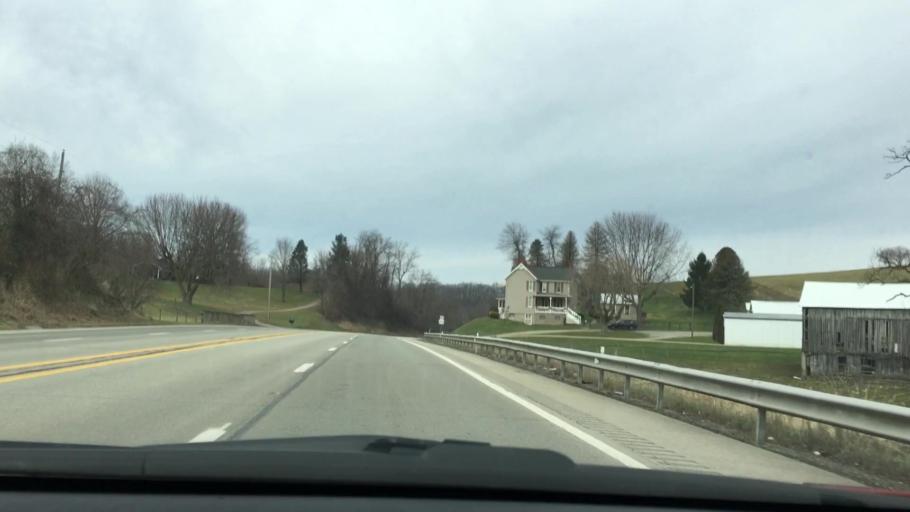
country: US
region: Pennsylvania
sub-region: Fayette County
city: Perryopolis
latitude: 40.0440
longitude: -79.7730
